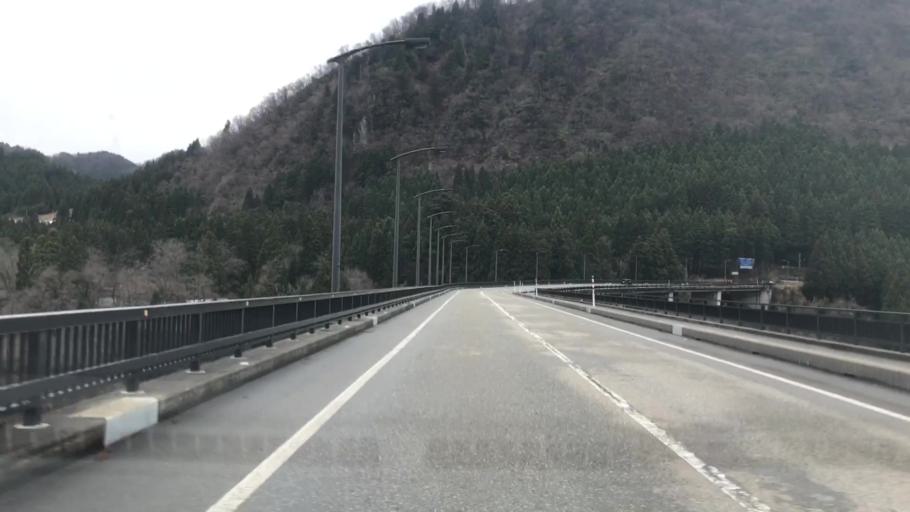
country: JP
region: Toyama
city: Kamiichi
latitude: 36.5797
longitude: 137.4068
